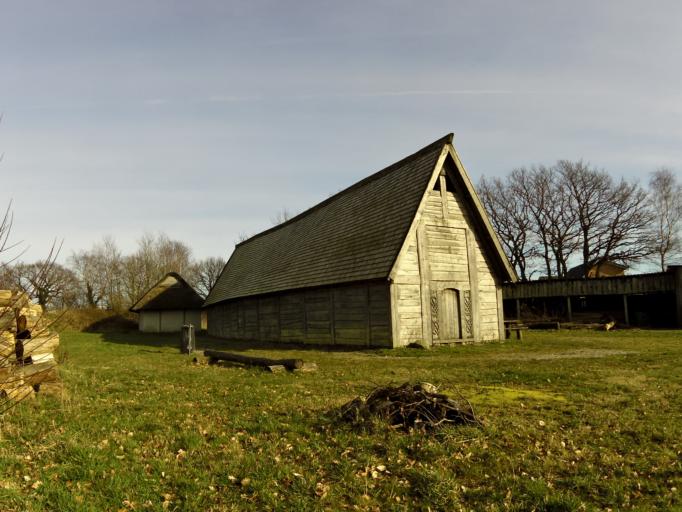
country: DK
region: South Denmark
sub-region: Kolding Kommune
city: Vamdrup
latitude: 55.3619
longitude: 9.2211
